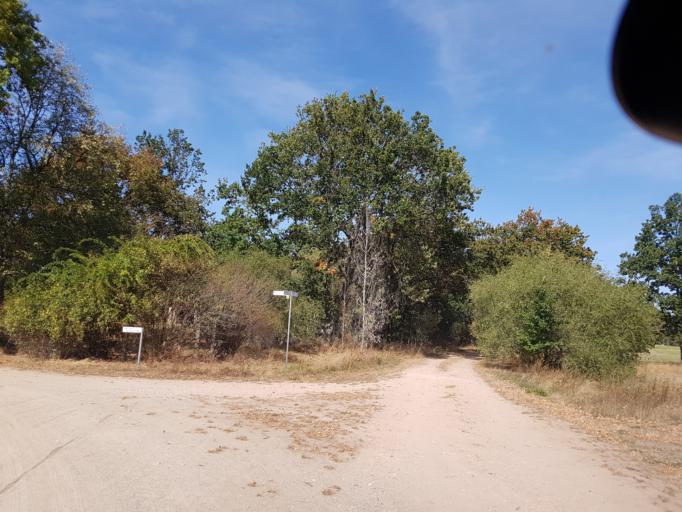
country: DE
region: Brandenburg
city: Luckau
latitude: 51.8670
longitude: 13.6461
